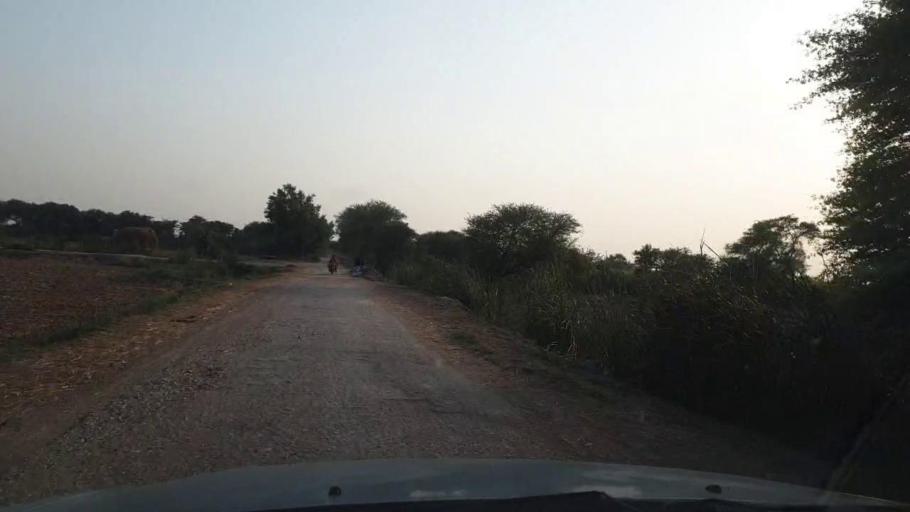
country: PK
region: Sindh
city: Tando Muhammad Khan
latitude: 25.0123
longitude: 68.4374
